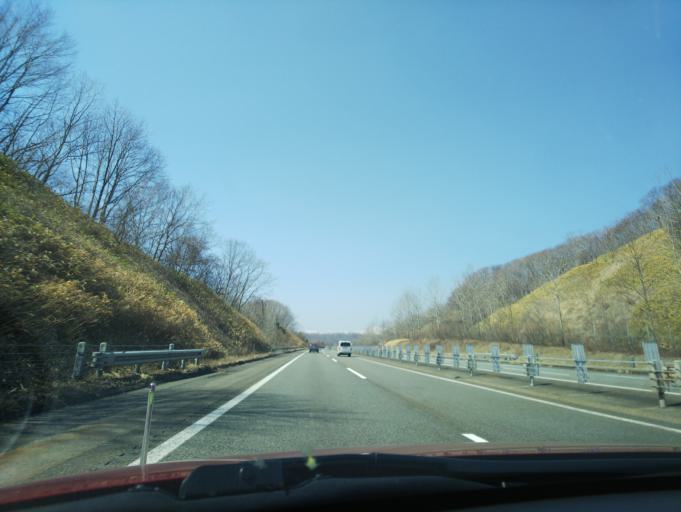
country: JP
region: Hokkaido
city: Shiraoi
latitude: 42.5772
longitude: 141.3882
